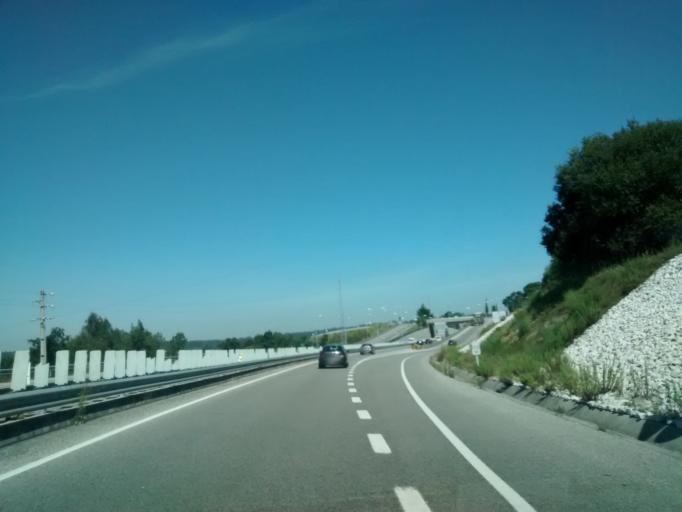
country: PT
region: Aveiro
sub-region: Oliveira do Bairro
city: Oliveira do Bairro
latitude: 40.5109
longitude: -8.4976
